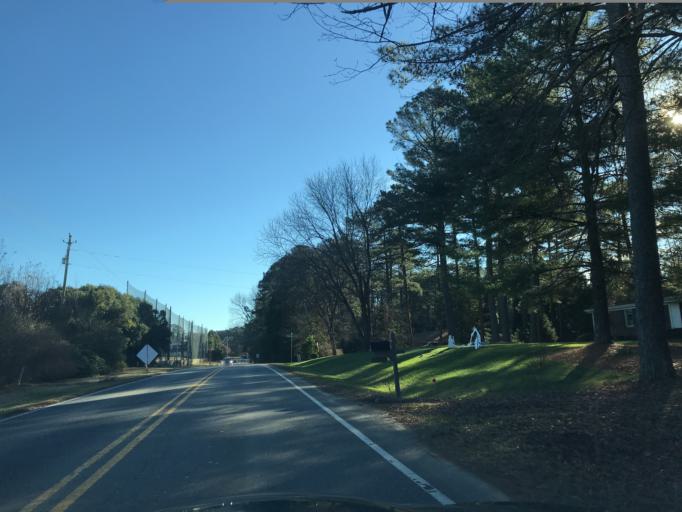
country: US
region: North Carolina
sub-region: Wake County
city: West Raleigh
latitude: 35.9055
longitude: -78.6944
